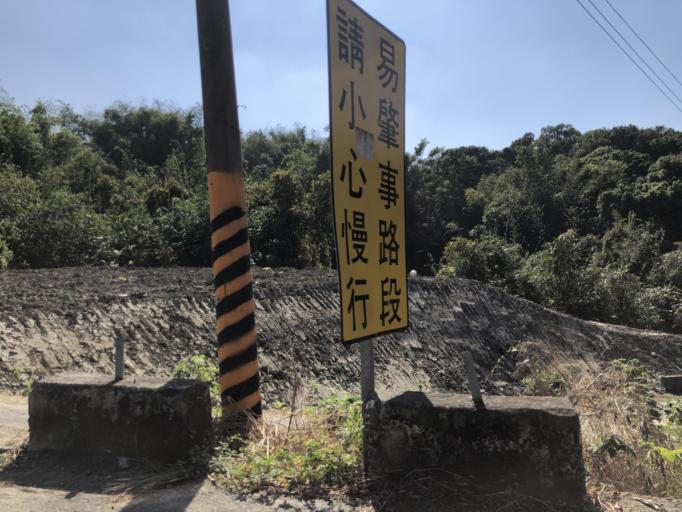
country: TW
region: Taiwan
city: Yujing
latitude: 23.0346
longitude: 120.3510
